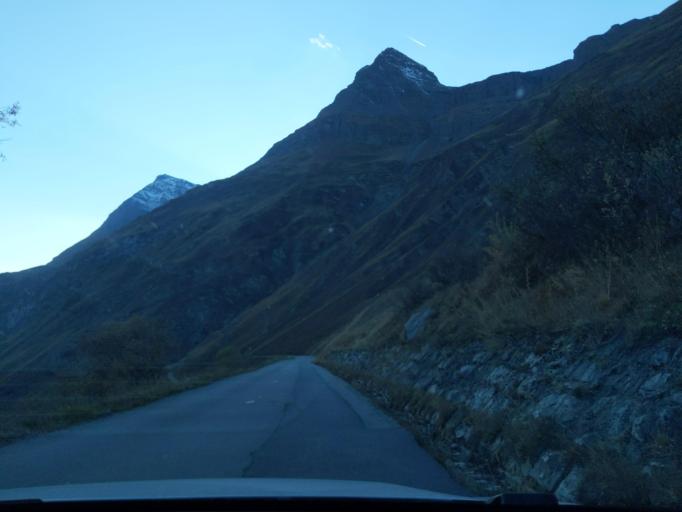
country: FR
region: Rhone-Alpes
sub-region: Departement de la Savoie
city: Val-d'Isere
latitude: 45.3747
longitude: 7.0392
